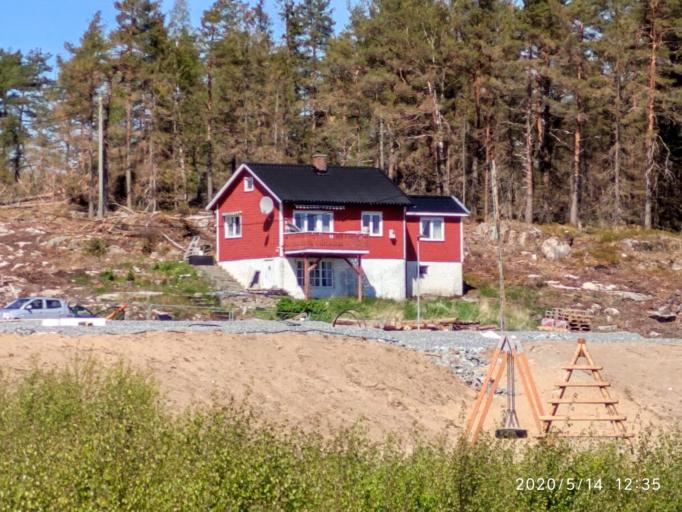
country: NO
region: Ostfold
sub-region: Halden
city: Halden
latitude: 59.1071
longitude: 11.4424
